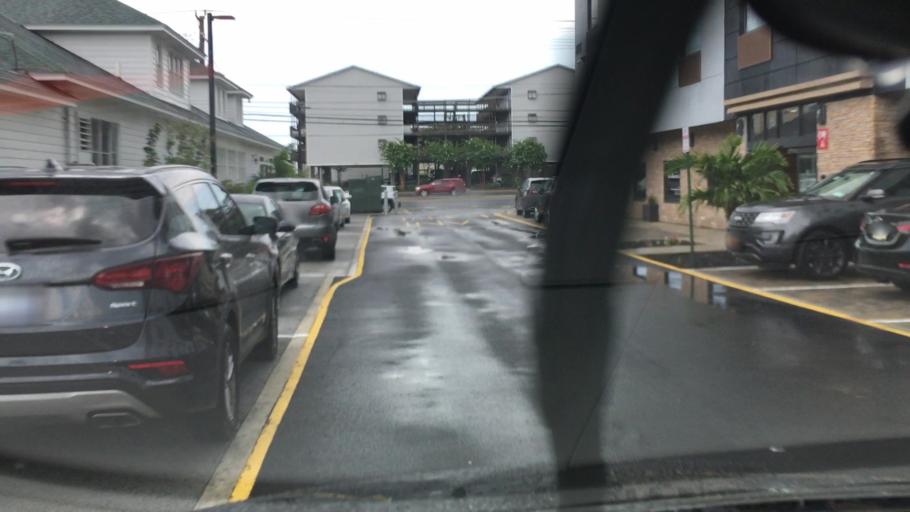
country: US
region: Maryland
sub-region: Worcester County
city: Ocean City
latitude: 38.4293
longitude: -75.0572
